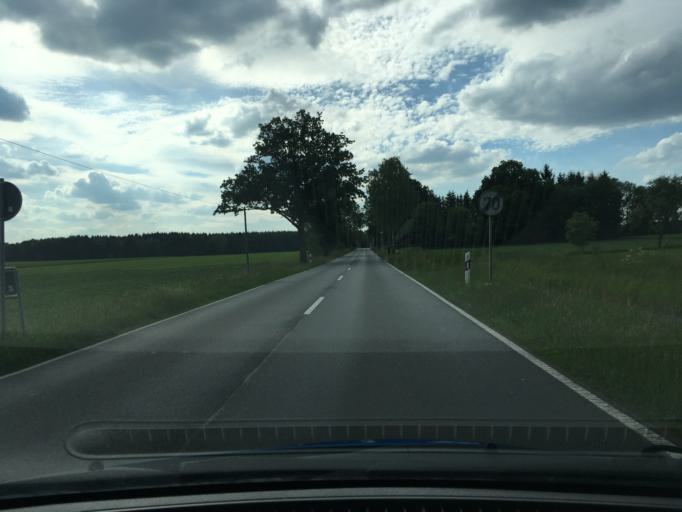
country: DE
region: Lower Saxony
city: Otter
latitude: 53.2519
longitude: 9.7657
